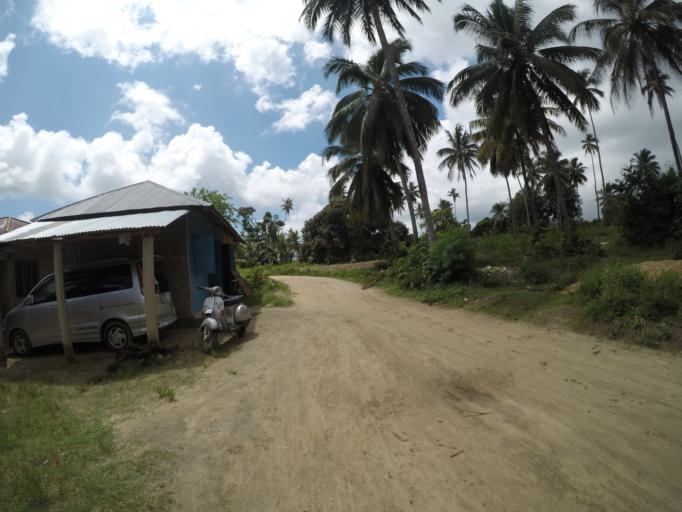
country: TZ
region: Pemba South
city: Mtambile
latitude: -5.3856
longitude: 39.7429
